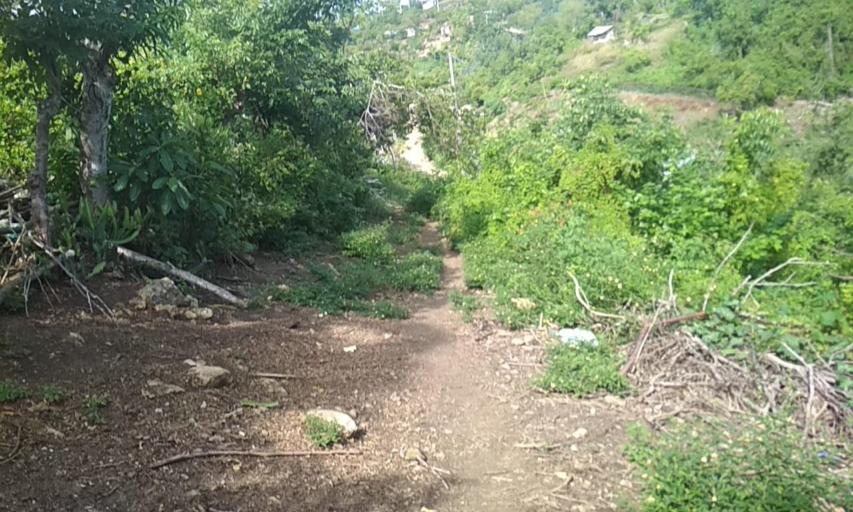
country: MX
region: Veracruz
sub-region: Papantla
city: Polutla
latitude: 20.5726
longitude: -97.1909
